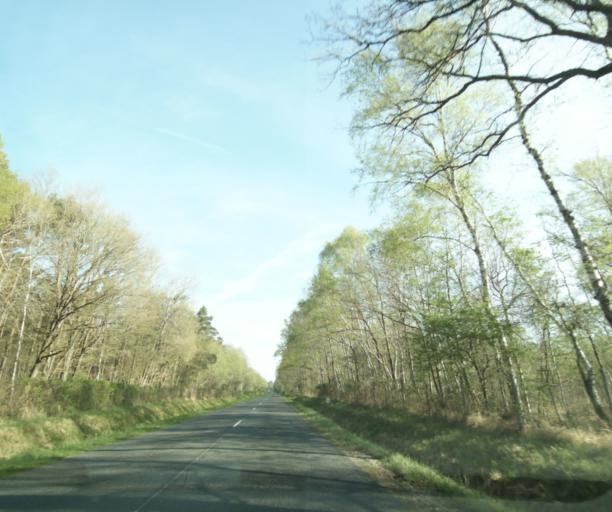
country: FR
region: Ile-de-France
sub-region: Departement de Seine-et-Marne
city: Vernou-la-Celle-sur-Seine
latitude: 48.4257
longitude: 2.8491
